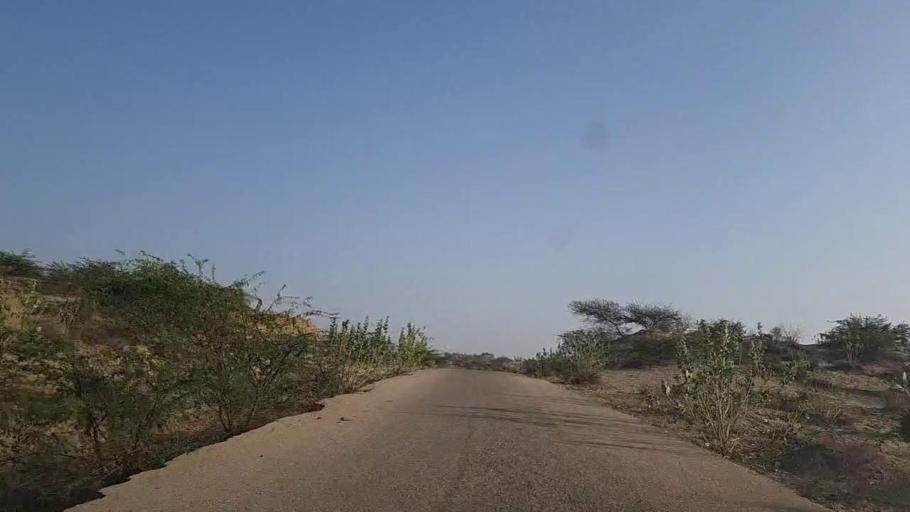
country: PK
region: Sindh
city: Diplo
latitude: 24.6049
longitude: 69.3794
